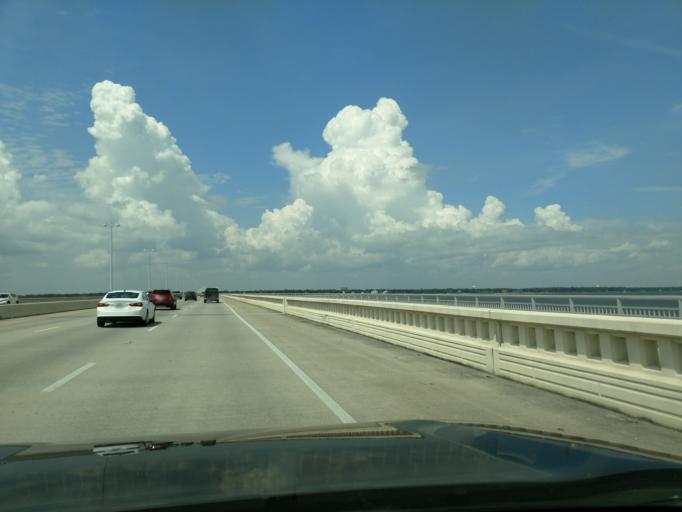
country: US
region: Mississippi
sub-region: Harrison County
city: Biloxi
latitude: 30.3952
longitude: -88.8548
